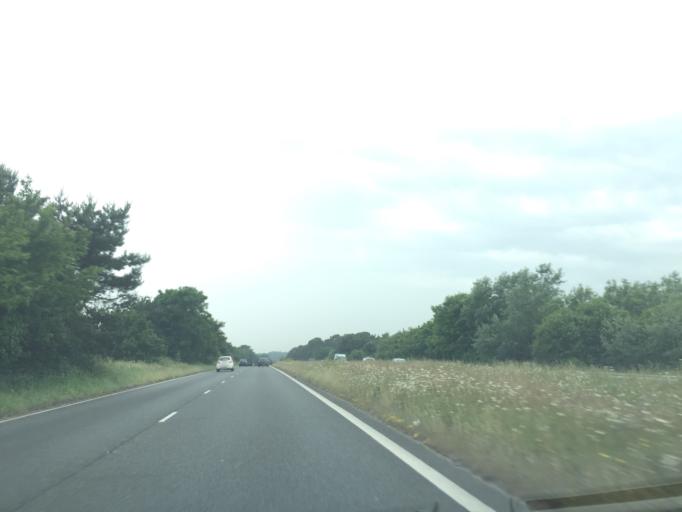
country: GB
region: England
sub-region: Dorset
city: Broadstone
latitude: 50.7392
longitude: -2.0122
